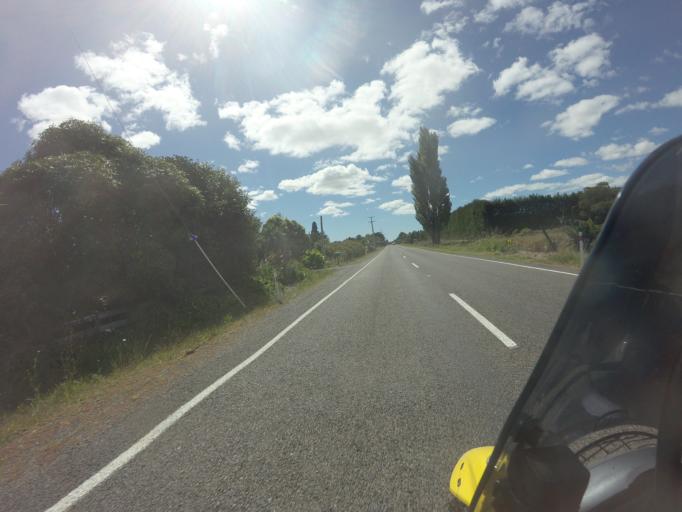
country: NZ
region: Bay of Plenty
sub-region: Whakatane District
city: Edgecumbe
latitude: -38.0398
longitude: 176.8322
